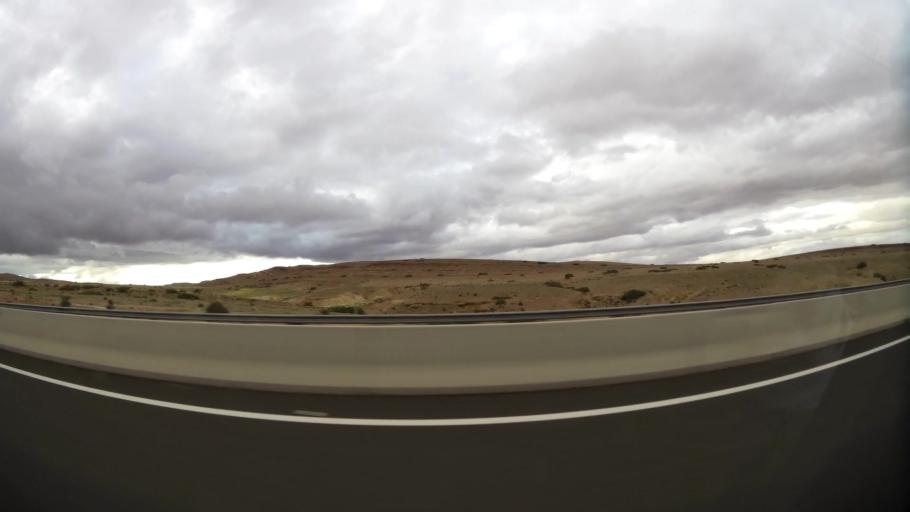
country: MA
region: Taza-Al Hoceima-Taounate
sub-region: Taza
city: Taza
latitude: 34.3060
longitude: -3.6846
